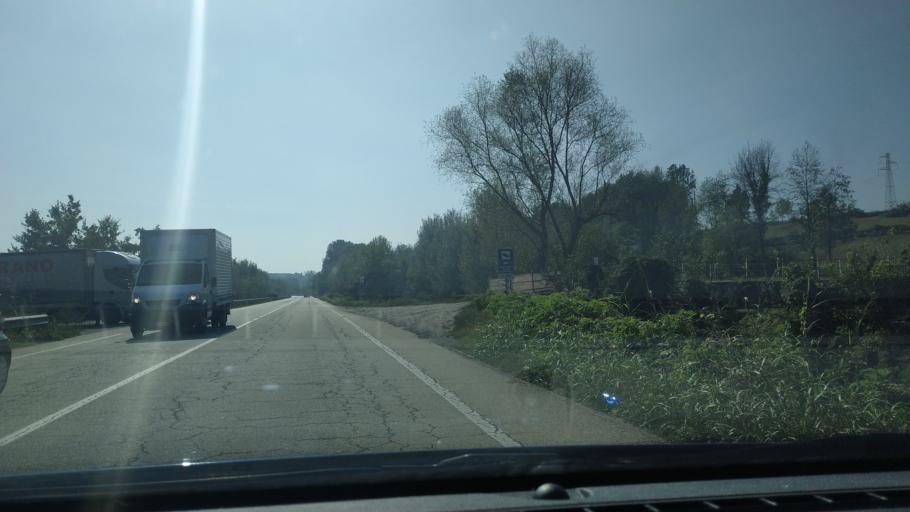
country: IT
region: Piedmont
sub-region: Provincia di Alessandria
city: Valenza
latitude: 45.0355
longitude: 8.6282
